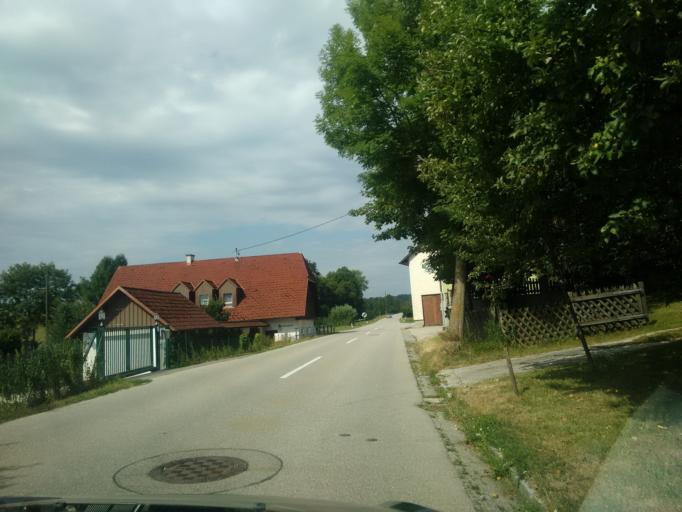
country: AT
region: Upper Austria
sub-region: Politischer Bezirk Grieskirchen
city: Bad Schallerbach
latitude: 48.1969
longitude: 13.9170
